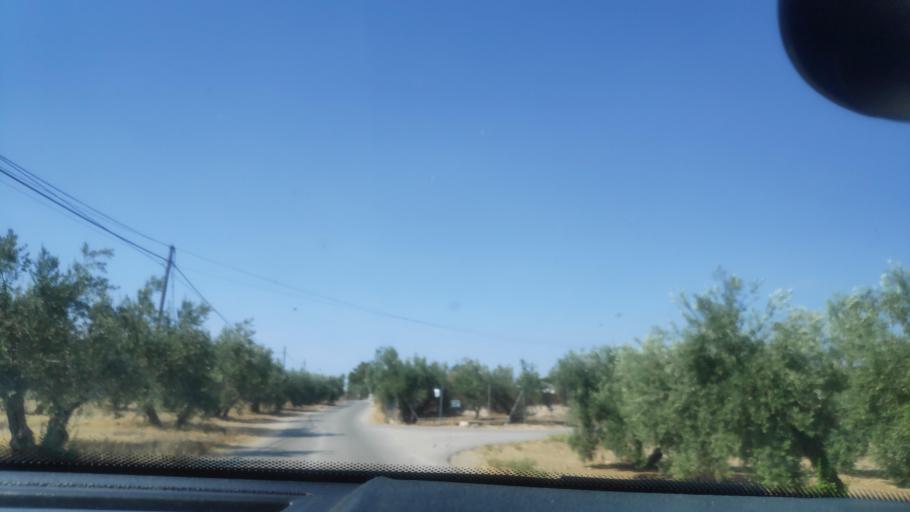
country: ES
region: Andalusia
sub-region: Provincia de Jaen
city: Jaen
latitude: 37.8270
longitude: -3.7587
